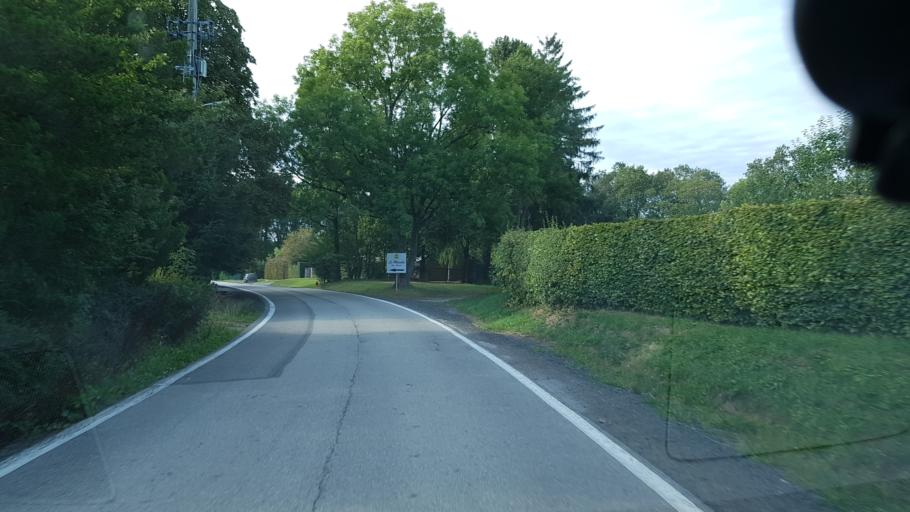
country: BE
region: Wallonia
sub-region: Province de Liege
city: Theux
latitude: 50.4978
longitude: 5.7699
